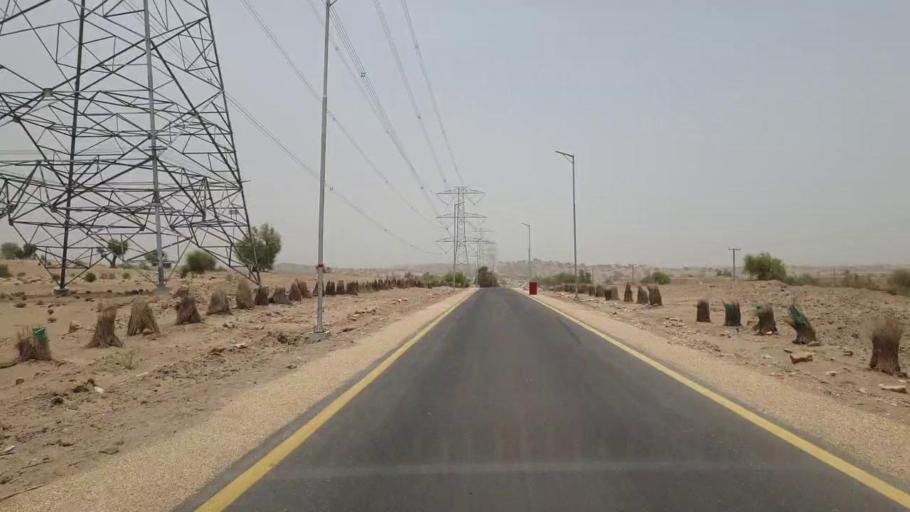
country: PK
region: Sindh
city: Islamkot
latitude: 24.7272
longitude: 70.3158
